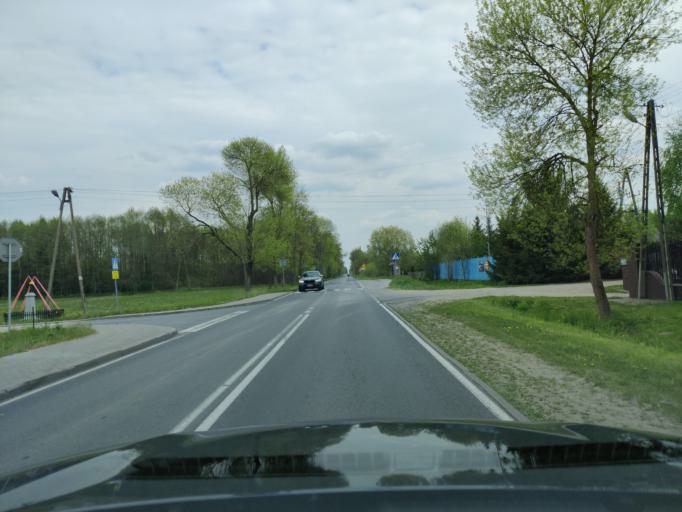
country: PL
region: Masovian Voivodeship
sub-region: Powiat wyszkowski
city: Rzasnik
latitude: 52.6193
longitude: 21.3606
